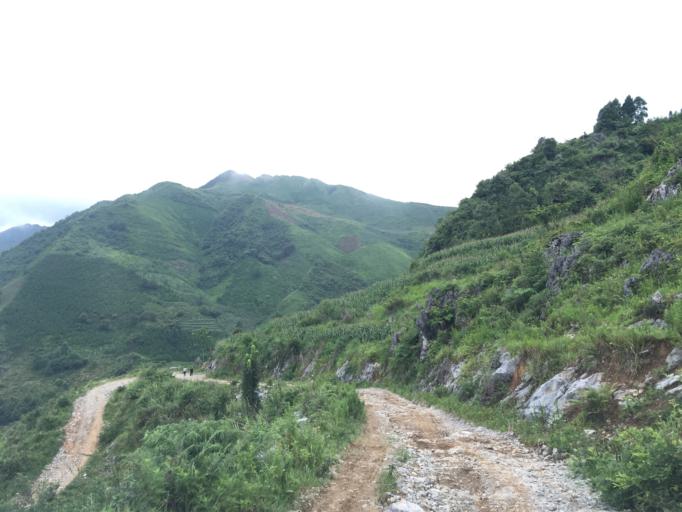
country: CN
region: Guangxi Zhuangzu Zizhiqu
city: Xinzhou
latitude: 24.9911
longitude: 105.6371
